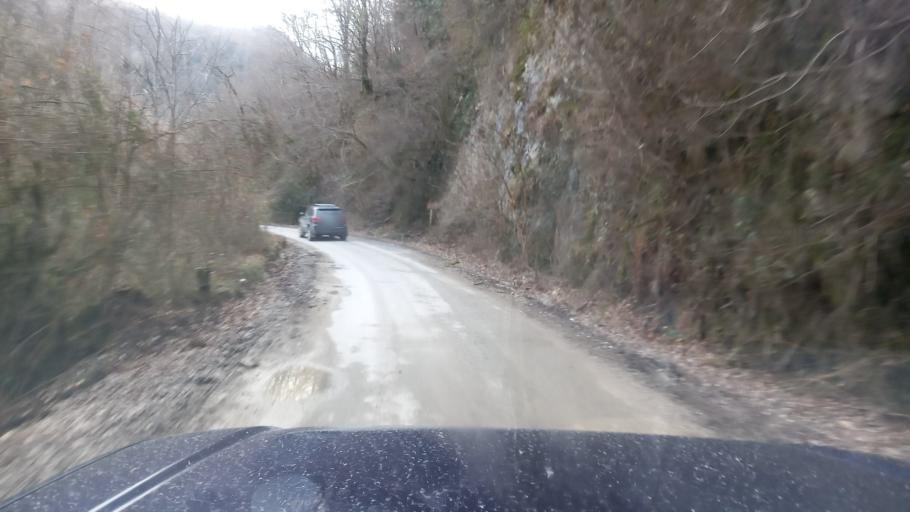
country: GE
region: Abkhazia
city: Gulrip'shi
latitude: 43.0178
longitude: 41.2284
